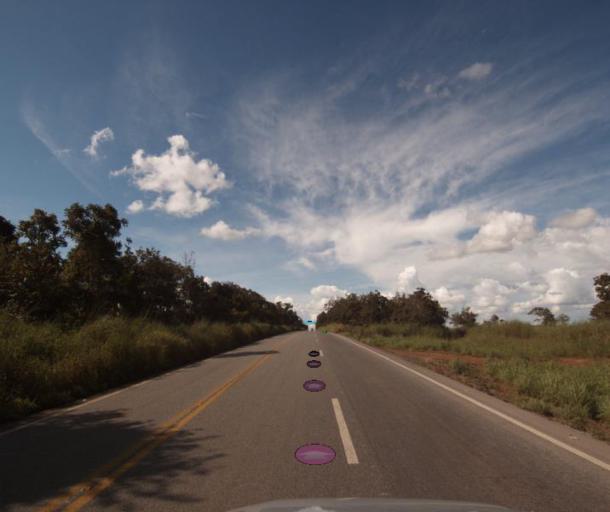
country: BR
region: Goias
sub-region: Porangatu
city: Porangatu
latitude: -13.0681
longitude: -49.1846
